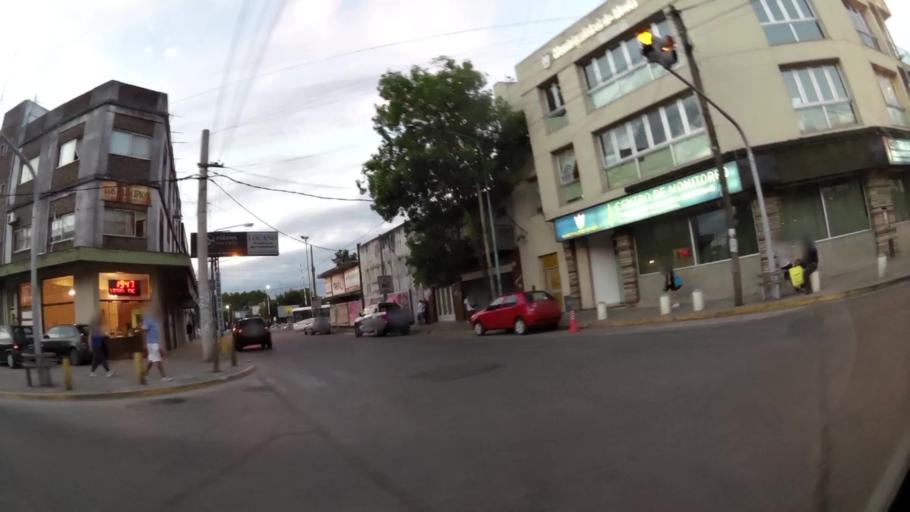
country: AR
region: Buenos Aires
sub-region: Partido de Merlo
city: Merlo
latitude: -34.6650
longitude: -58.7300
